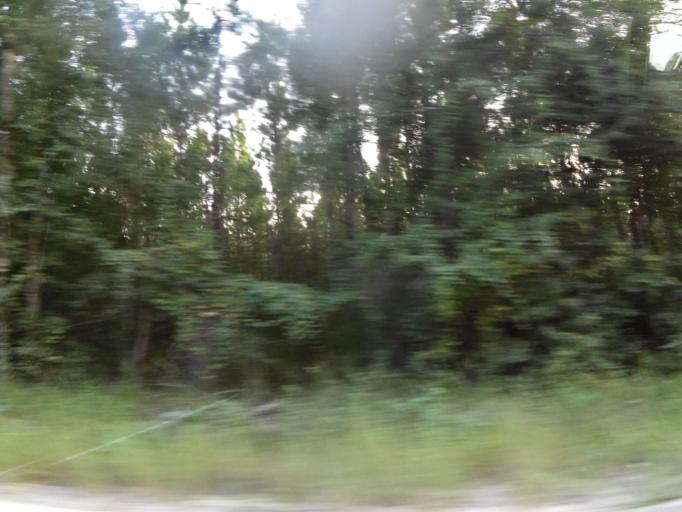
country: US
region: Florida
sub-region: Duval County
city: Baldwin
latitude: 30.3866
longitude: -82.0469
